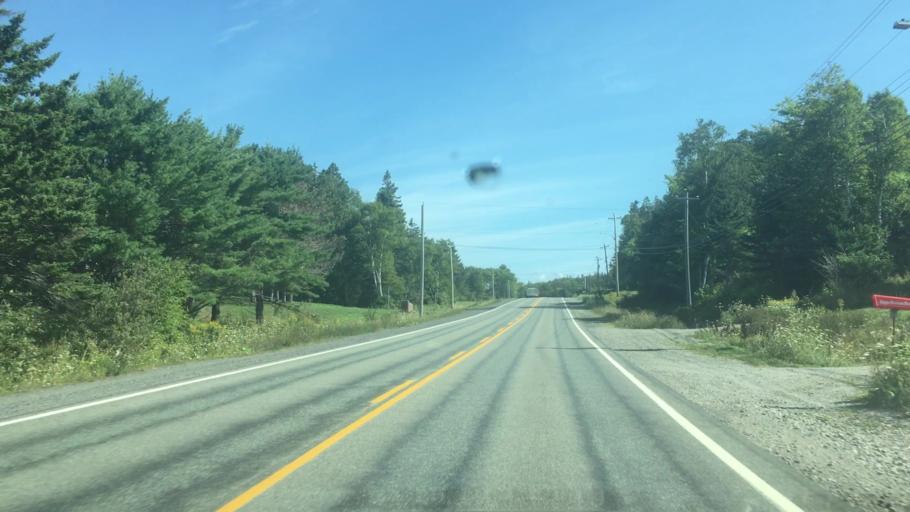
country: CA
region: Nova Scotia
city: Sydney
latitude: 45.9943
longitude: -60.4083
